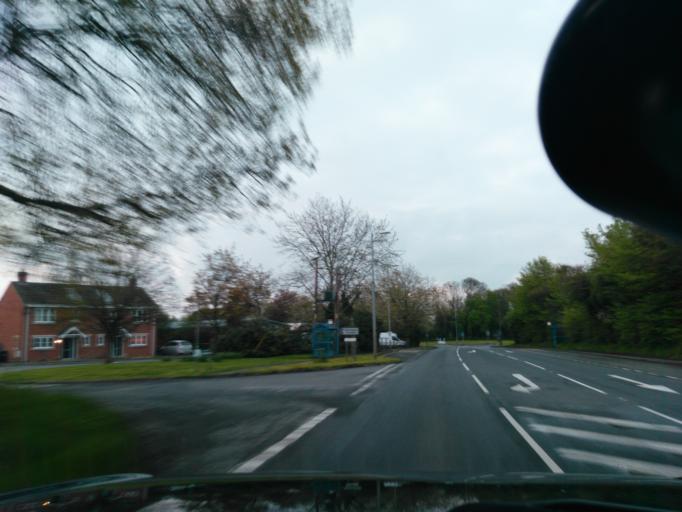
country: GB
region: England
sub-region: Wiltshire
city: Melksham
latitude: 51.3398
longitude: -2.1509
